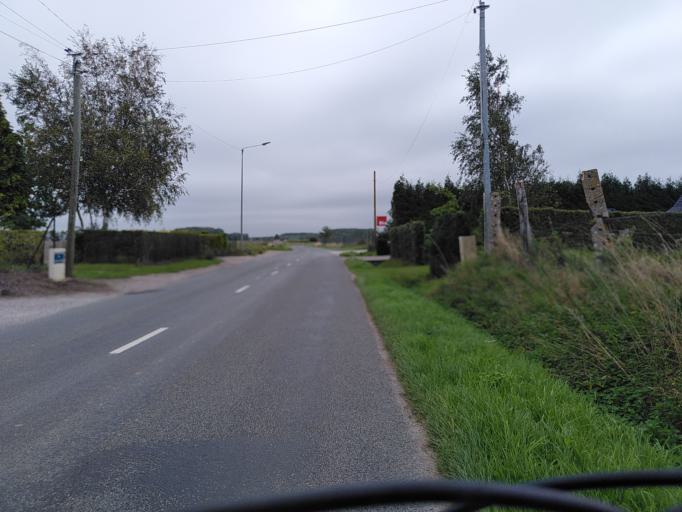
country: FR
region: Nord-Pas-de-Calais
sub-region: Departement du Pas-de-Calais
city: Mametz
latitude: 50.6452
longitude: 2.3127
